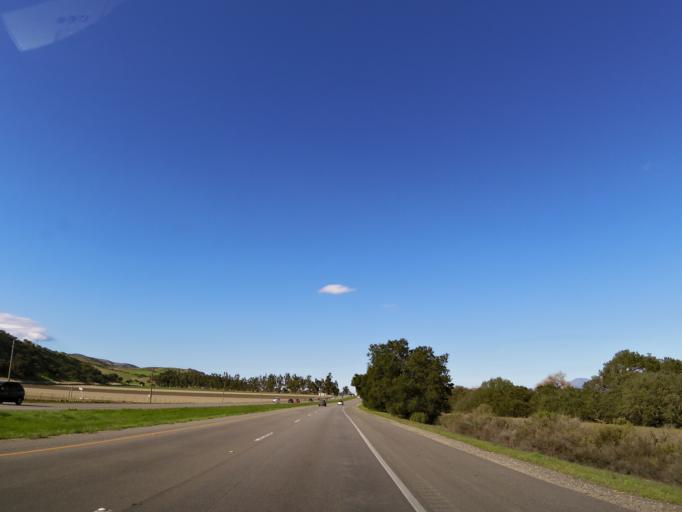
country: US
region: California
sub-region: Monterey County
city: King City
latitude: 36.2047
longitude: -121.1573
